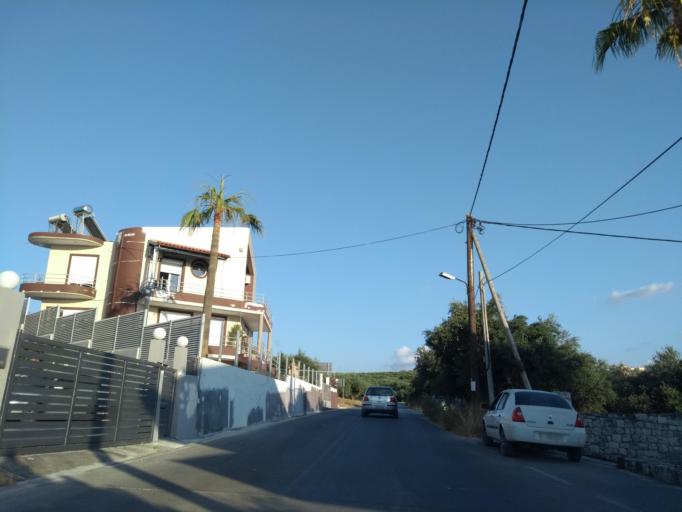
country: GR
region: Crete
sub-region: Nomos Chanias
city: Kalivai
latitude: 35.4483
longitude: 24.1752
